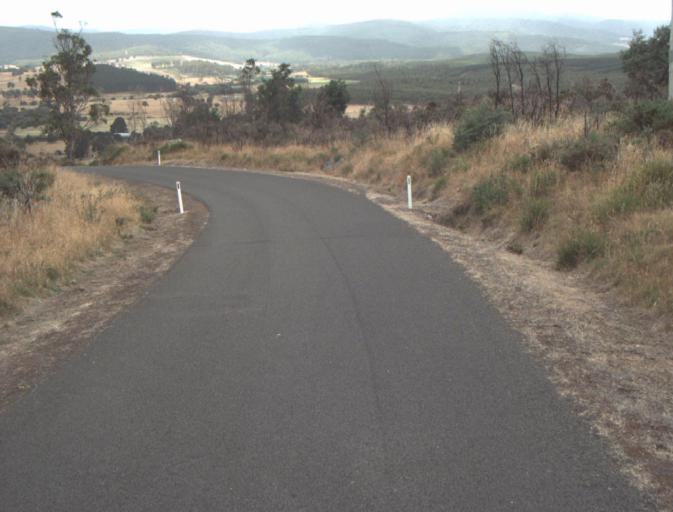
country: AU
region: Tasmania
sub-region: Northern Midlands
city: Evandale
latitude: -41.5121
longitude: 147.4743
